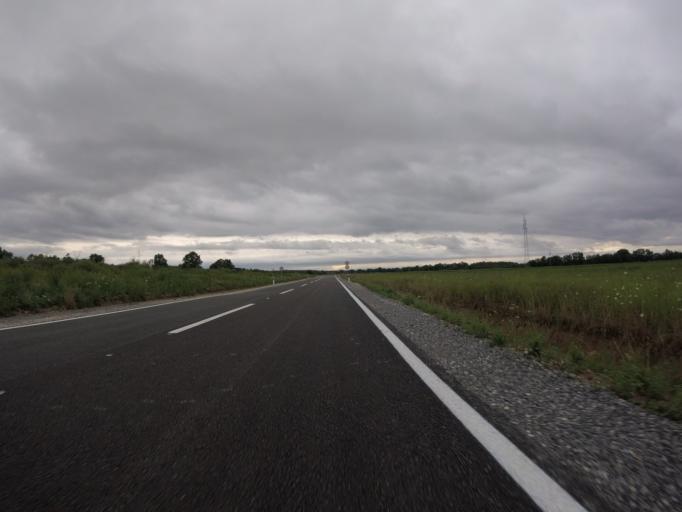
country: HR
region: Zagrebacka
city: Mraclin
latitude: 45.6569
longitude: 16.1047
